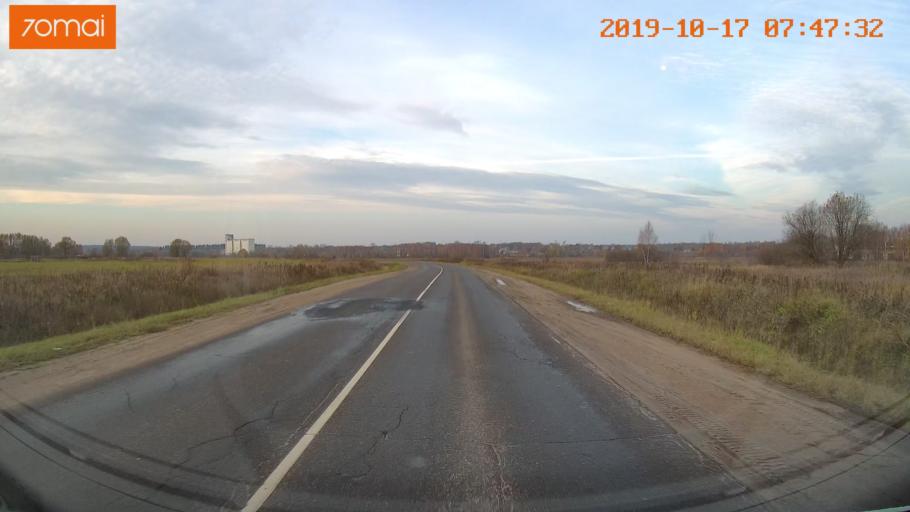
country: RU
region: Vladimir
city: Yur'yev-Pol'skiy
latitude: 56.4875
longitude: 39.6846
